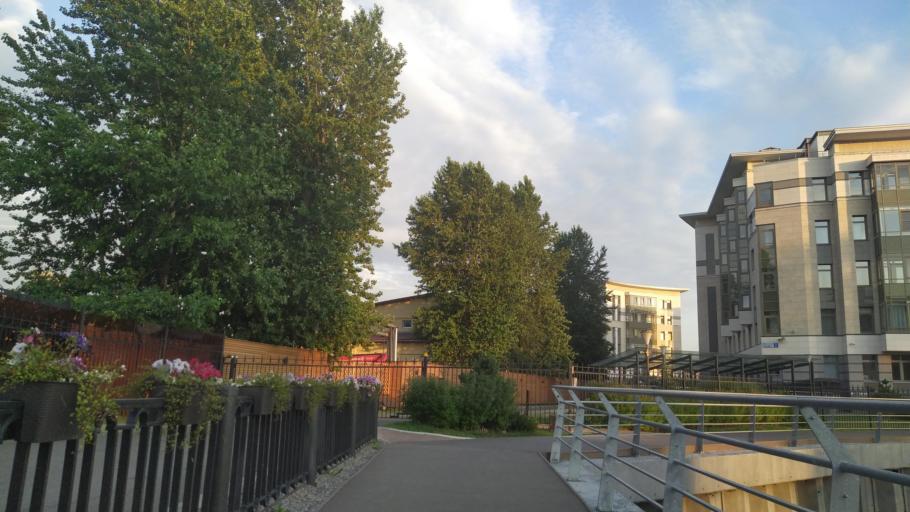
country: RU
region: Leningrad
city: Krestovskiy ostrov
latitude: 59.9544
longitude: 30.2802
